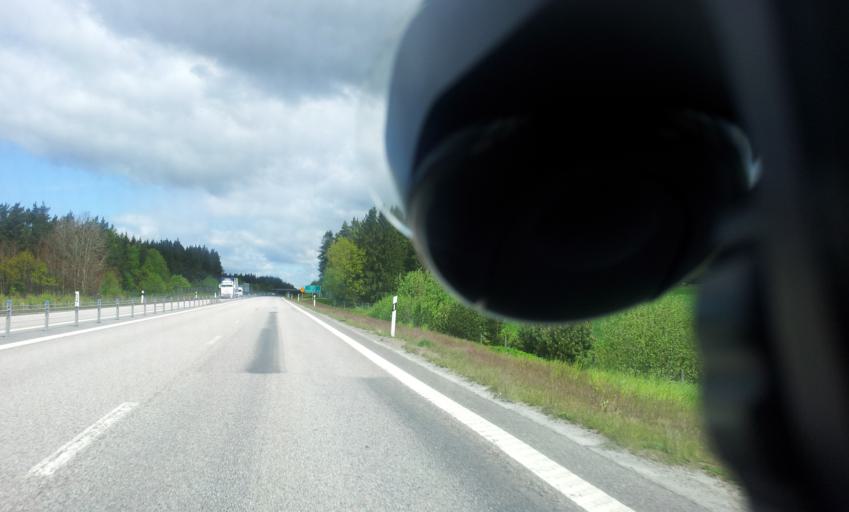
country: SE
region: Kalmar
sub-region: Torsas Kommun
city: Torsas
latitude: 56.4569
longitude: 16.0786
